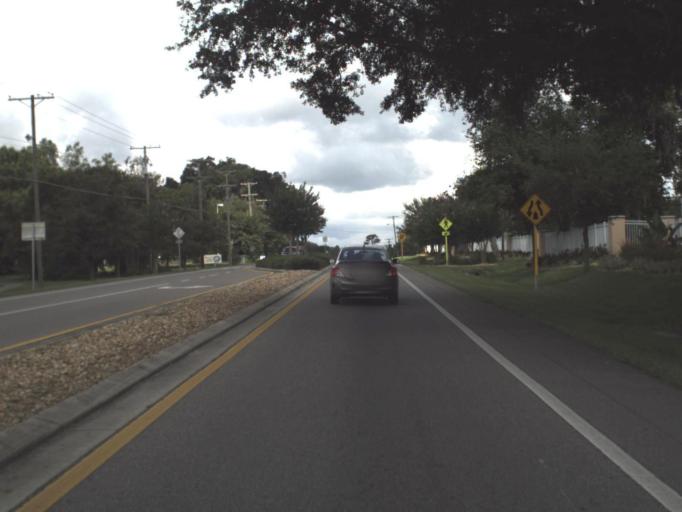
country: US
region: Florida
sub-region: Pasco County
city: Saint Leo
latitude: 28.3356
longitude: -82.2576
